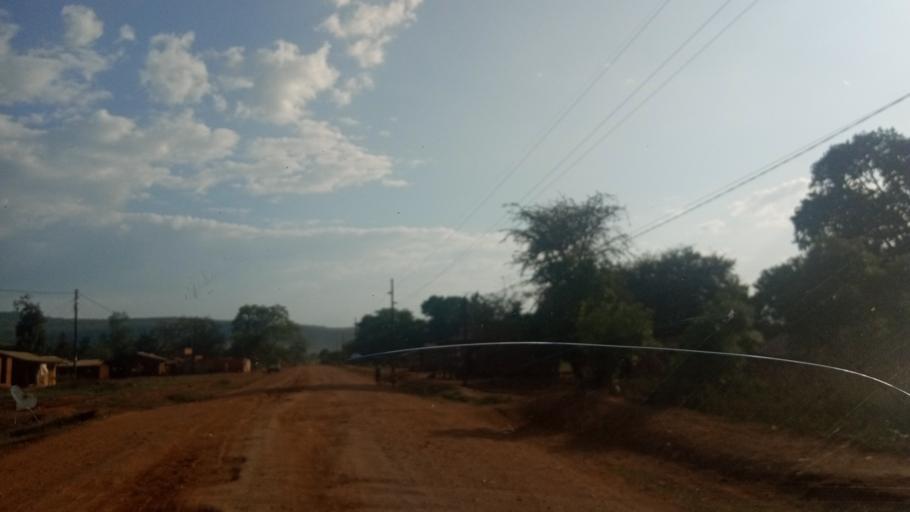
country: UG
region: Eastern Region
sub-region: Kapchorwa District
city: Kapchorwa
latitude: 1.4166
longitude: 34.3504
